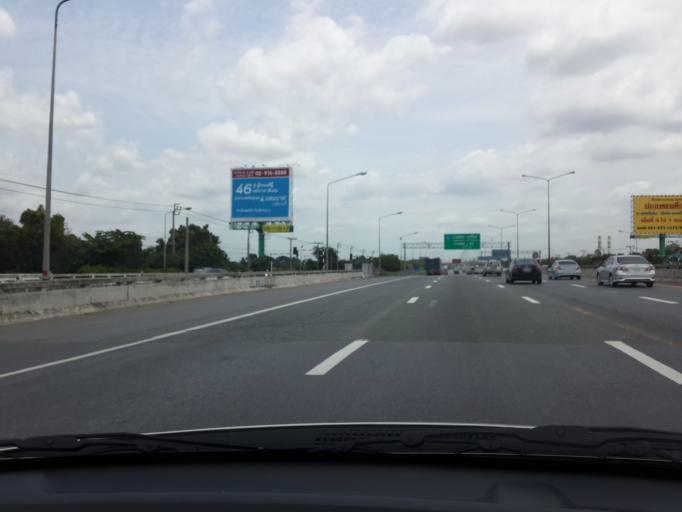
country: TH
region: Bangkok
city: Saphan Sung
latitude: 13.7597
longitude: 100.6969
